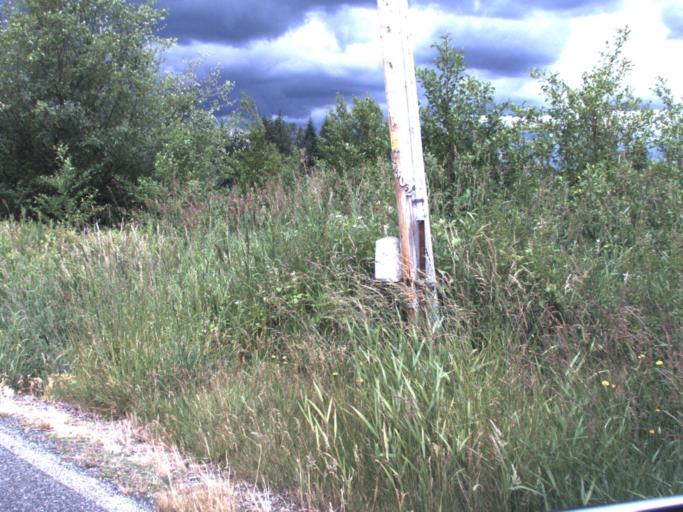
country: US
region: Washington
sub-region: Whatcom County
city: Birch Bay
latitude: 48.8940
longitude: -122.7265
